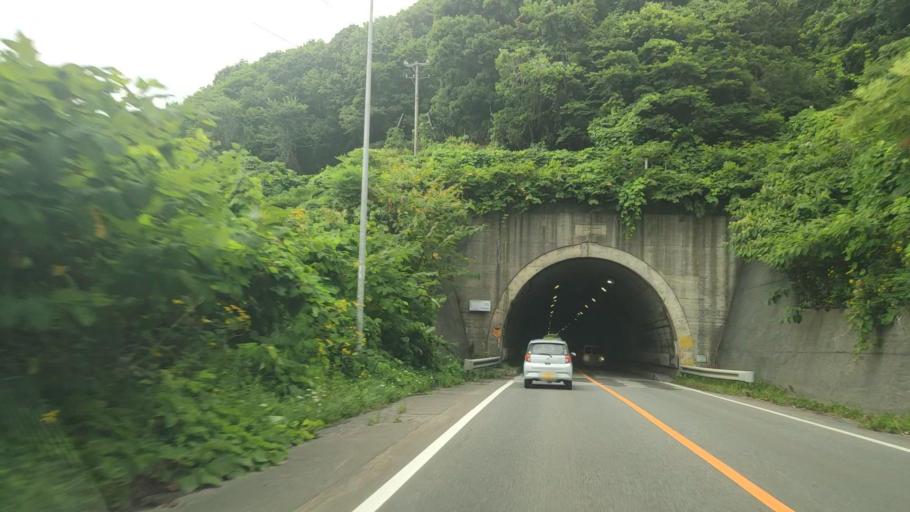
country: JP
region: Hokkaido
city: Date
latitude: 42.5703
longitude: 140.7340
